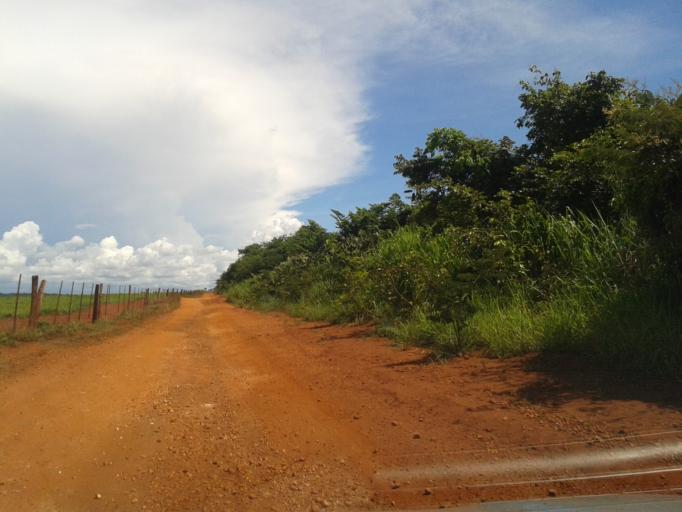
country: BR
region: Minas Gerais
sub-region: Capinopolis
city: Capinopolis
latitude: -18.7067
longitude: -49.7728
